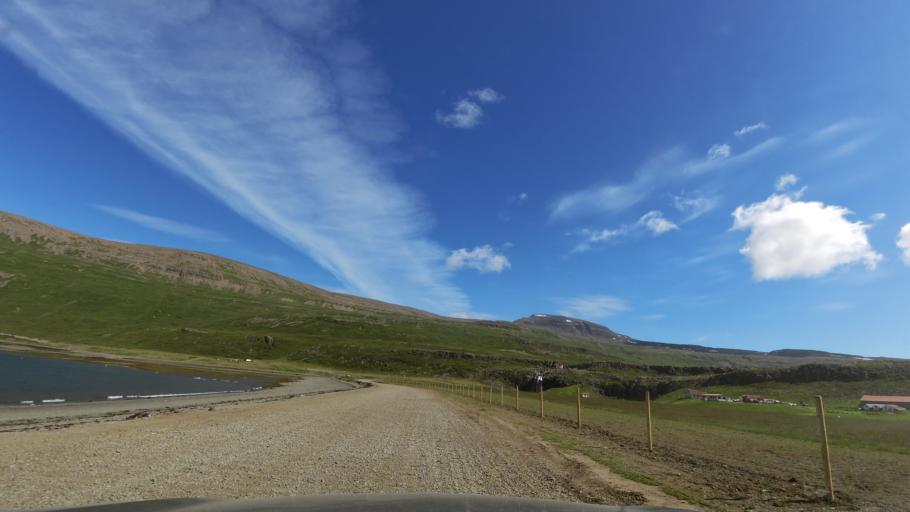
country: IS
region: Westfjords
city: Isafjoerdur
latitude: 65.6041
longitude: -23.5481
